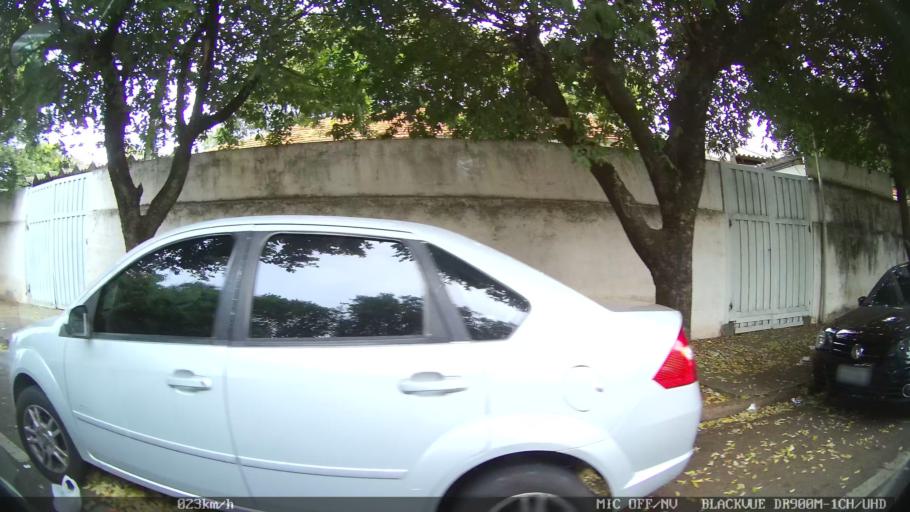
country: BR
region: Sao Paulo
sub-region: Sao Jose Do Rio Preto
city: Sao Jose do Rio Preto
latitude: -20.8308
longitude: -49.3958
